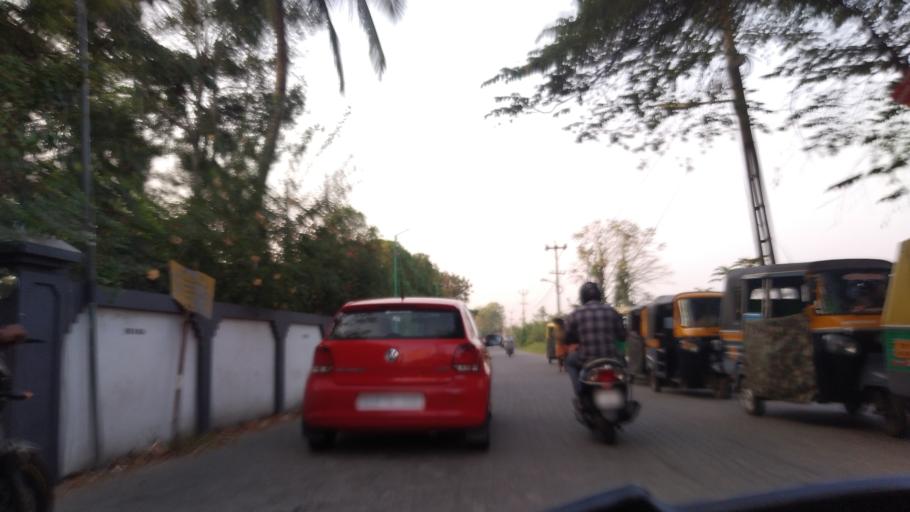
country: IN
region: Kerala
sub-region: Ernakulam
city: Elur
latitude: 10.0379
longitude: 76.2753
